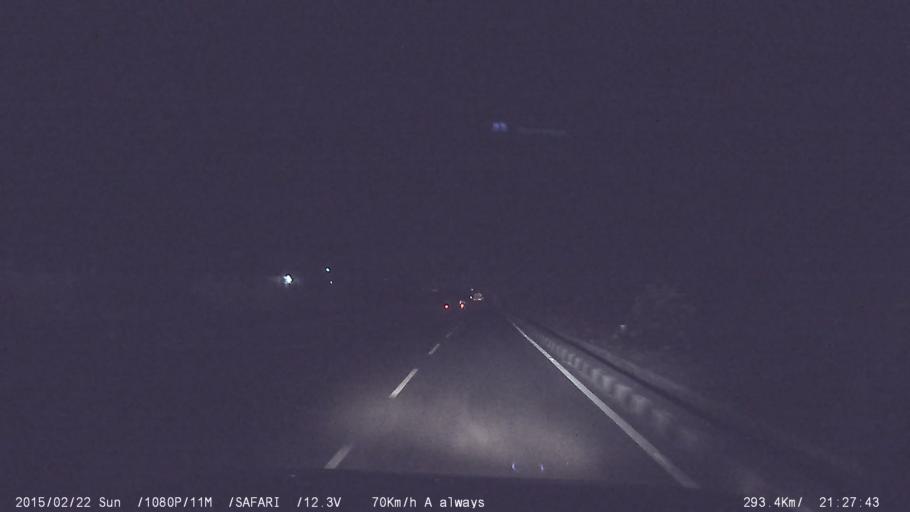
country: IN
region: Tamil Nadu
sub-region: Karur
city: Karur
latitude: 10.9181
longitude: 78.0434
